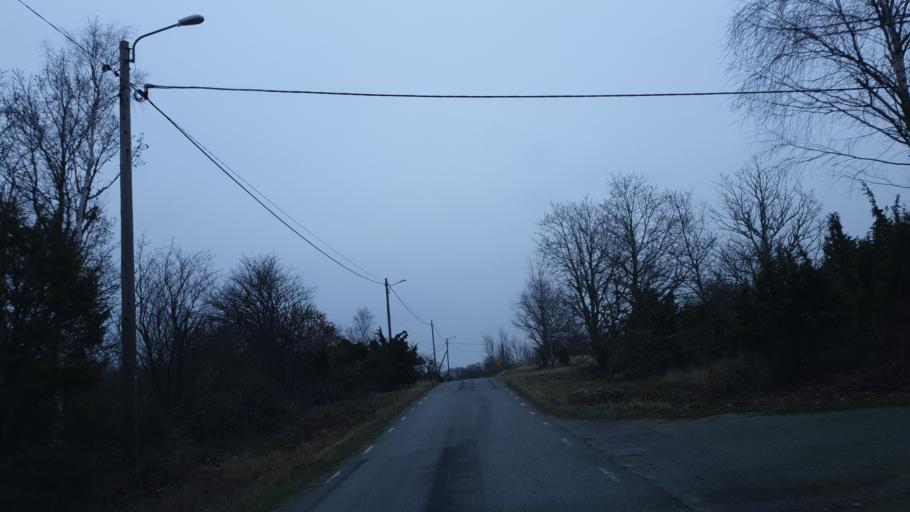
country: SE
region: Blekinge
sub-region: Karlskrona Kommun
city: Karlskrona
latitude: 56.1060
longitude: 15.5980
